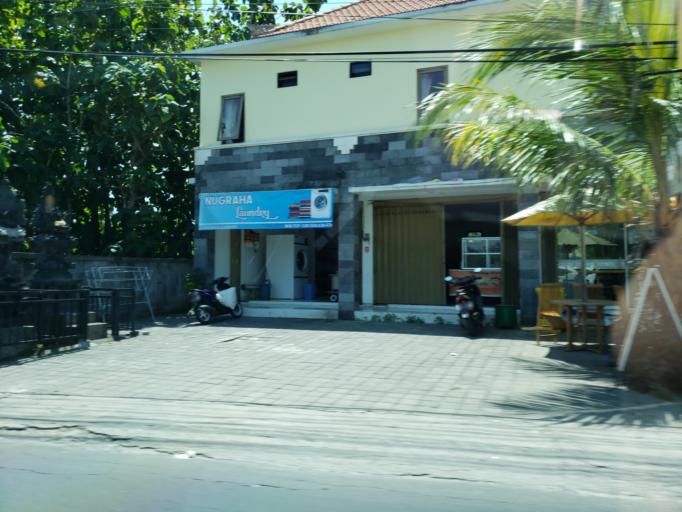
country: ID
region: Bali
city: Kangin
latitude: -8.8308
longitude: 115.1296
